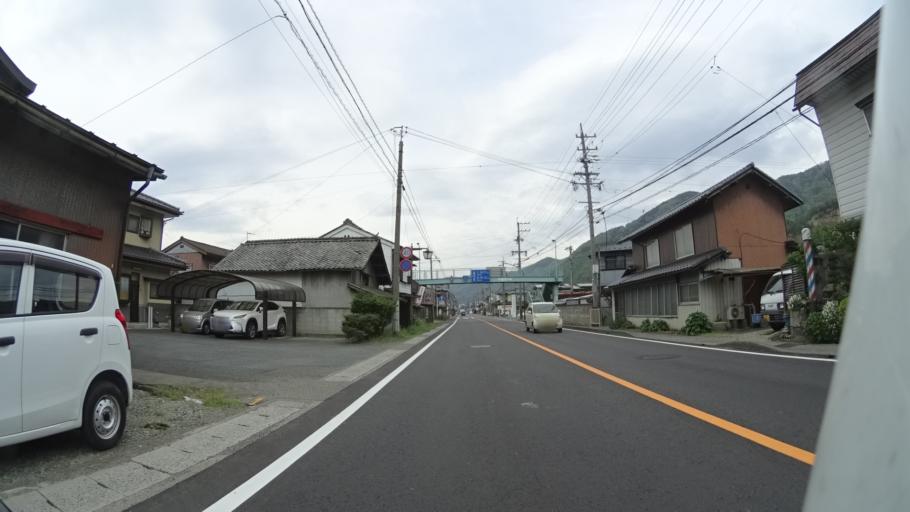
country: JP
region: Nagano
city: Ueda
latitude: 36.4873
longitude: 138.1531
